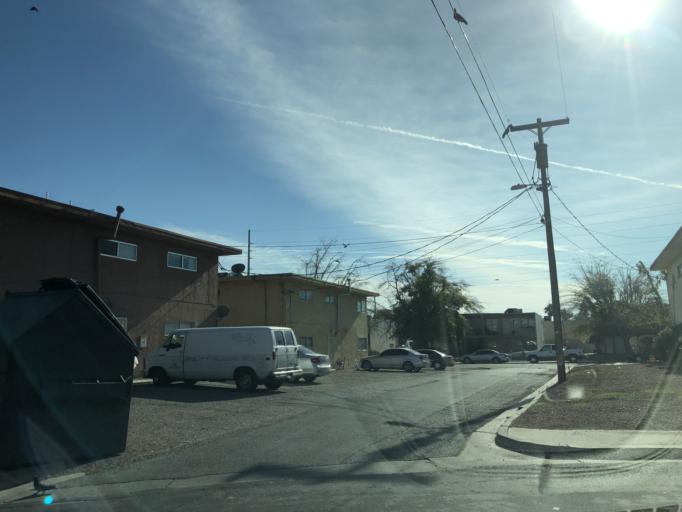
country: US
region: Nevada
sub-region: Clark County
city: Winchester
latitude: 36.1312
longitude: -115.1351
